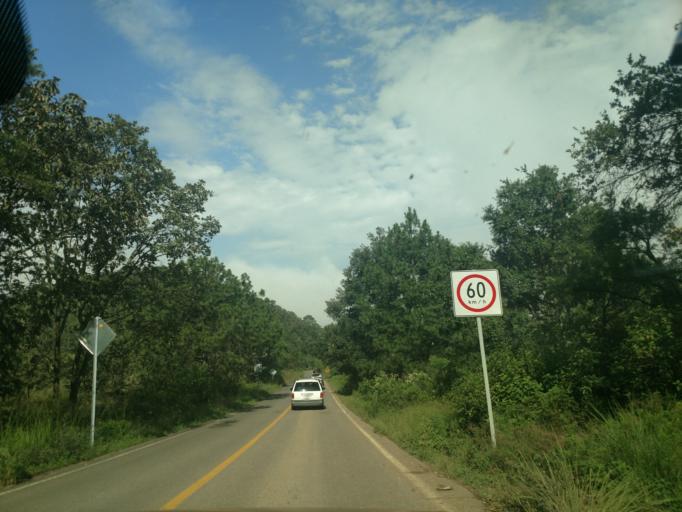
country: MX
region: Jalisco
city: El Salto
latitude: 20.4618
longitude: -104.3806
